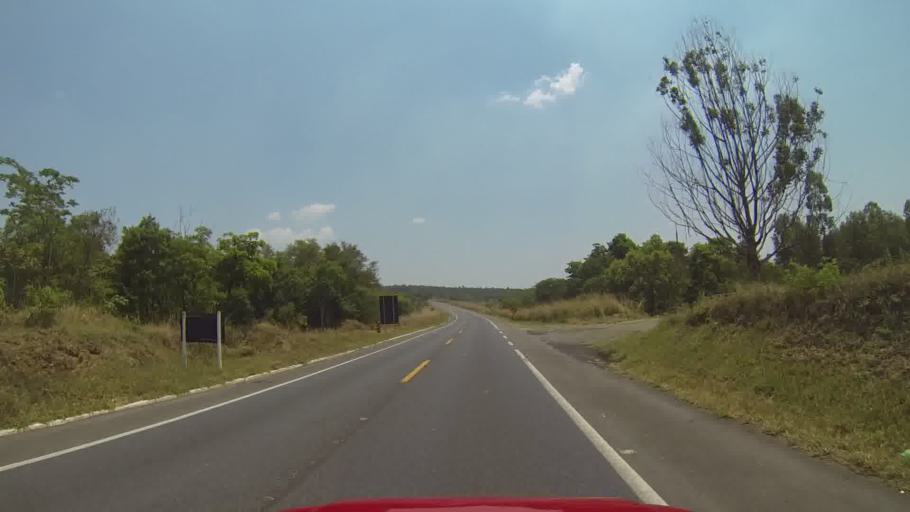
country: BR
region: Minas Gerais
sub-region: Formiga
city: Formiga
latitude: -20.3496
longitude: -45.3113
